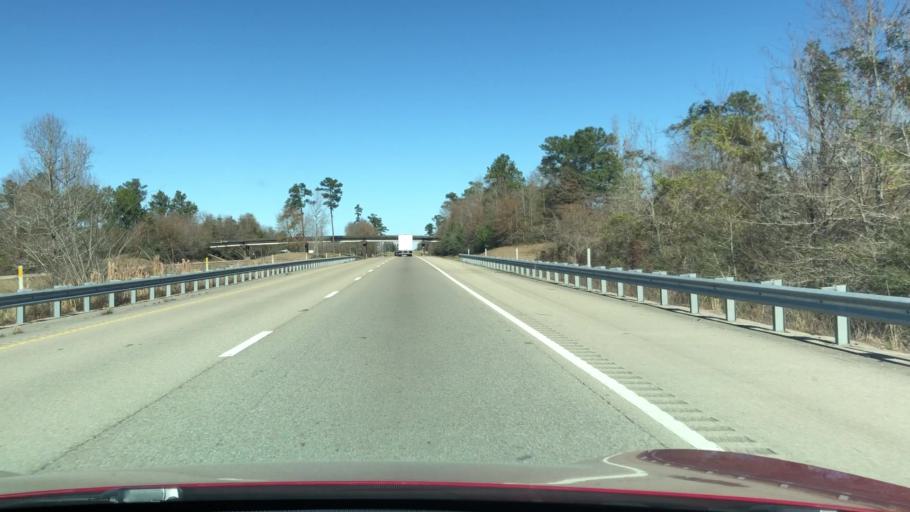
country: US
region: Mississippi
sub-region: Pearl River County
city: Poplarville
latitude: 30.7619
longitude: -89.5213
